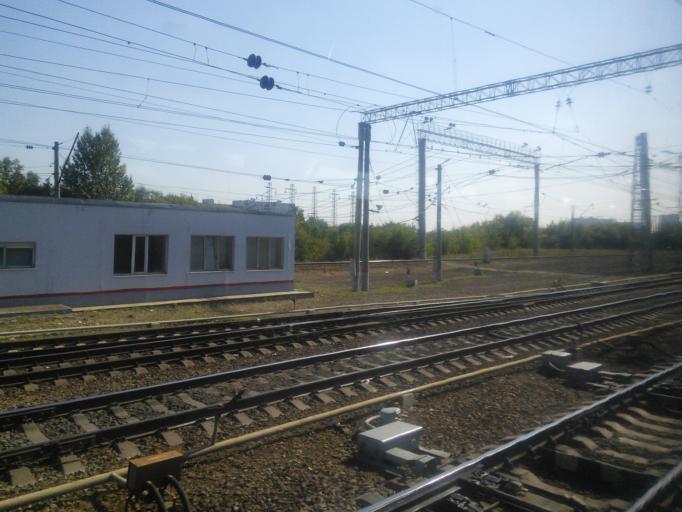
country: RU
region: Moskovskaya
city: Kur'yanovo
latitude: 55.6537
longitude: 37.7082
